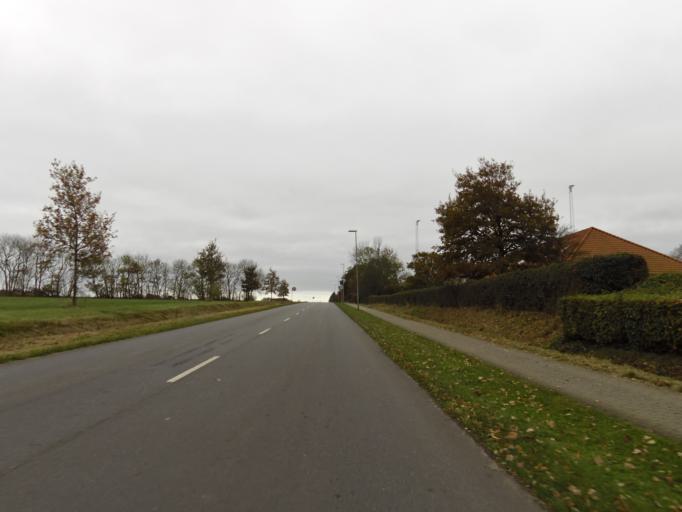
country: DK
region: South Denmark
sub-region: Haderslev Kommune
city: Gram
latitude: 55.2899
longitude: 9.0567
